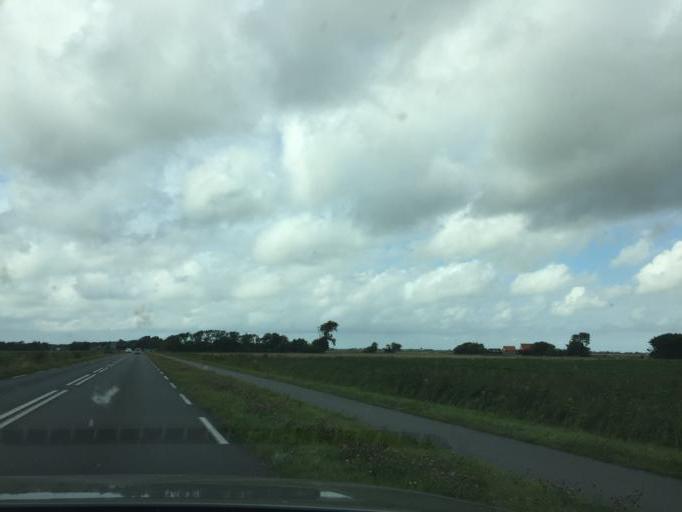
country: NL
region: North Holland
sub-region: Gemeente Texel
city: Den Burg
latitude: 53.0650
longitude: 4.7759
